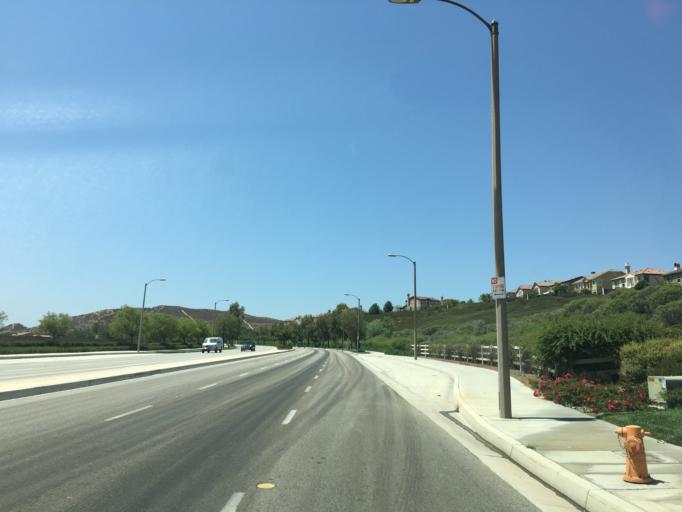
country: US
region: California
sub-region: Los Angeles County
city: Valencia
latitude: 34.4608
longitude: -118.5632
